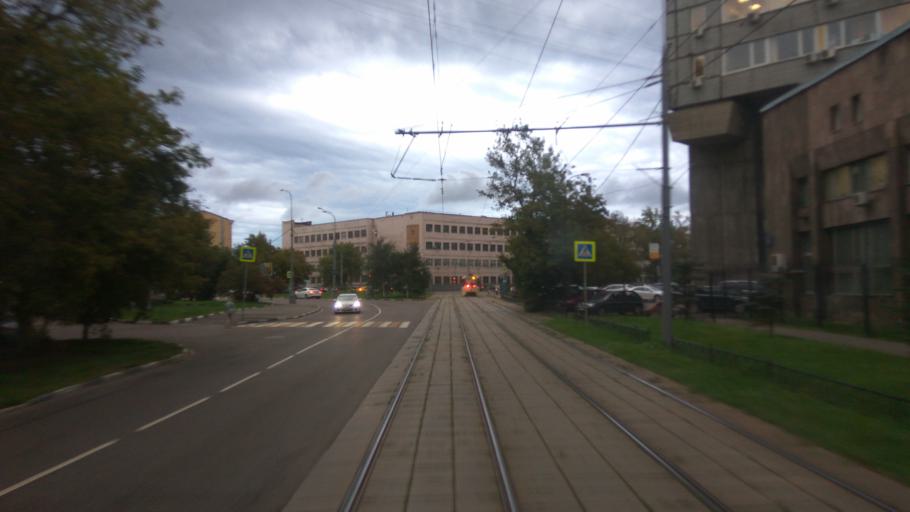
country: RU
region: Moscow
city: Taganskiy
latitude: 55.7213
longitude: 37.6720
